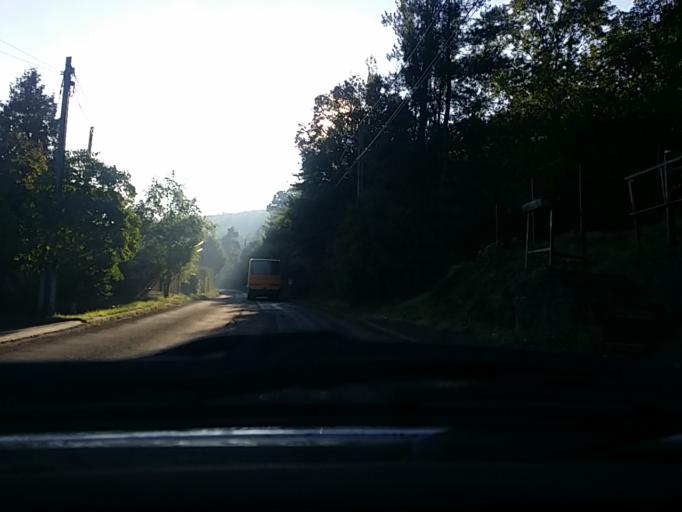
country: HU
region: Pest
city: Visegrad
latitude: 47.7199
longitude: 18.9892
